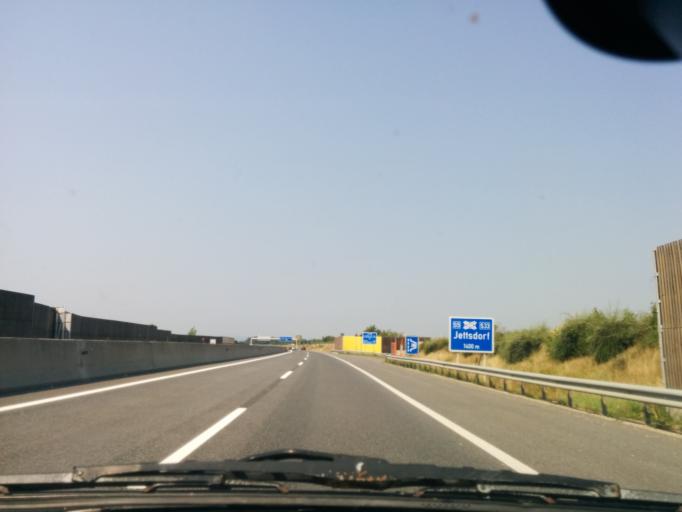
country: AT
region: Lower Austria
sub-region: Politischer Bezirk Tulln
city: Grafenworth
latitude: 48.4118
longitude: 15.7676
